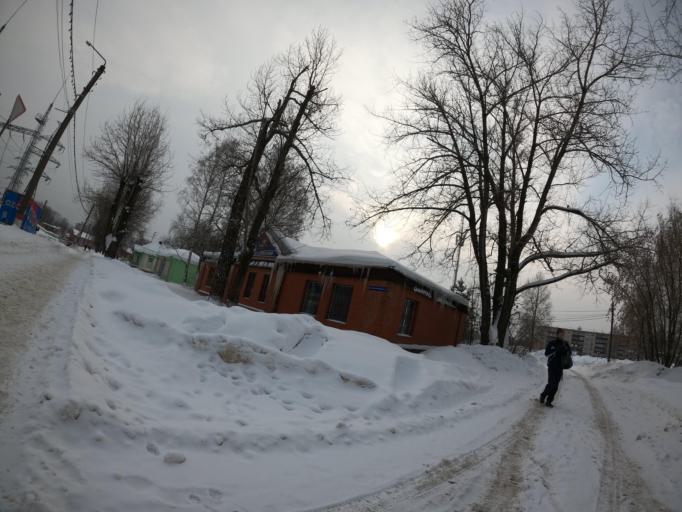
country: RU
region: Moskovskaya
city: Elektrogorsk
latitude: 55.8853
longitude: 38.7827
